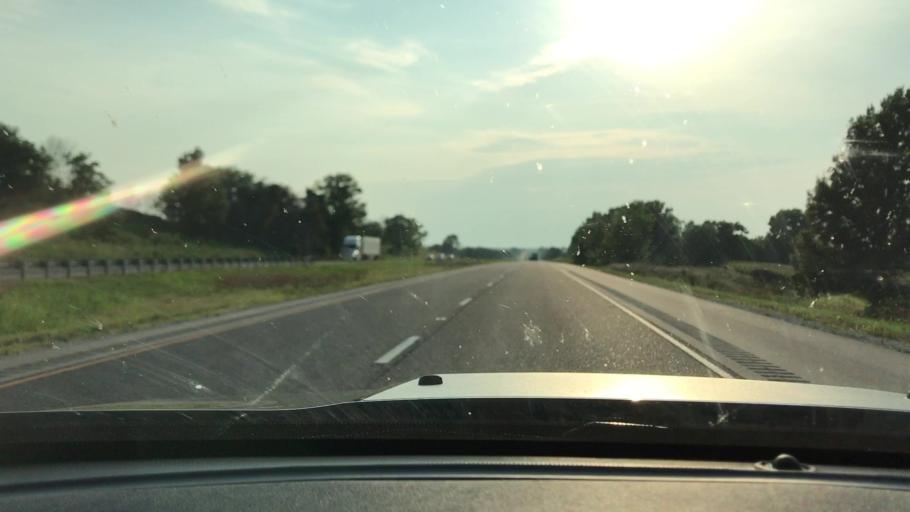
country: US
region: Illinois
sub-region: Henry County
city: Geneseo
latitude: 41.4146
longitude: -90.0691
